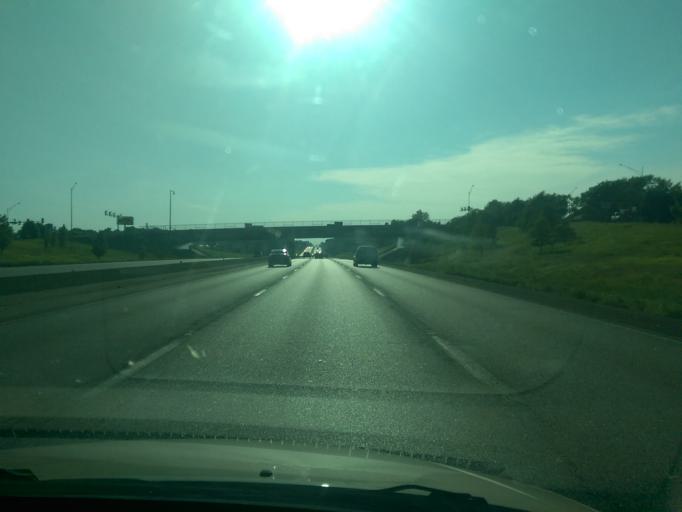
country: US
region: Missouri
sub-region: Jackson County
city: Independence
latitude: 39.0448
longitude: -94.3852
